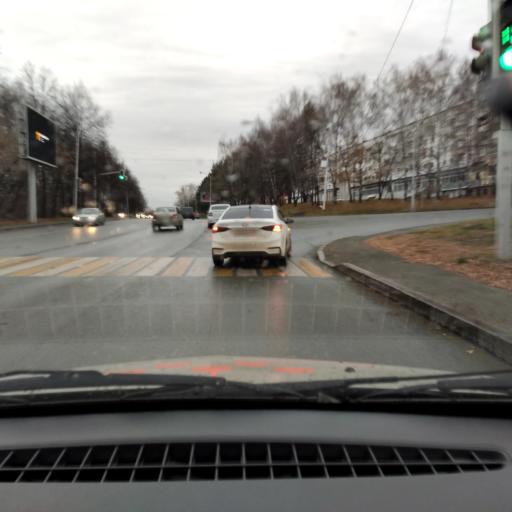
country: RU
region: Bashkortostan
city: Ufa
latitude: 54.8118
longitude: 56.0708
